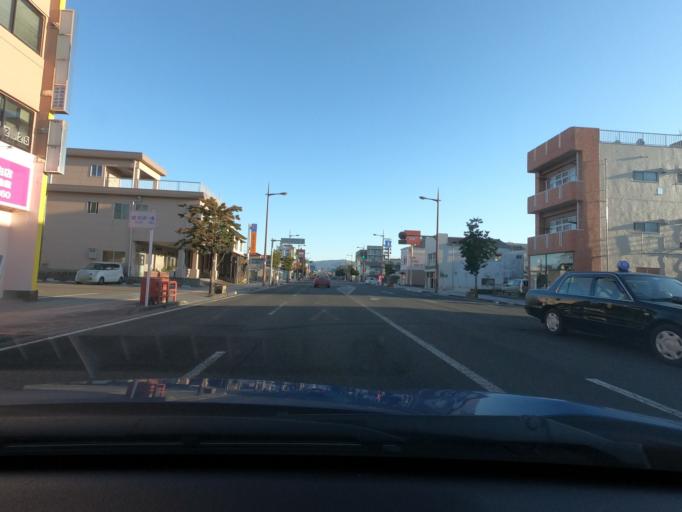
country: JP
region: Kagoshima
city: Satsumasendai
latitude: 31.8238
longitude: 130.3013
